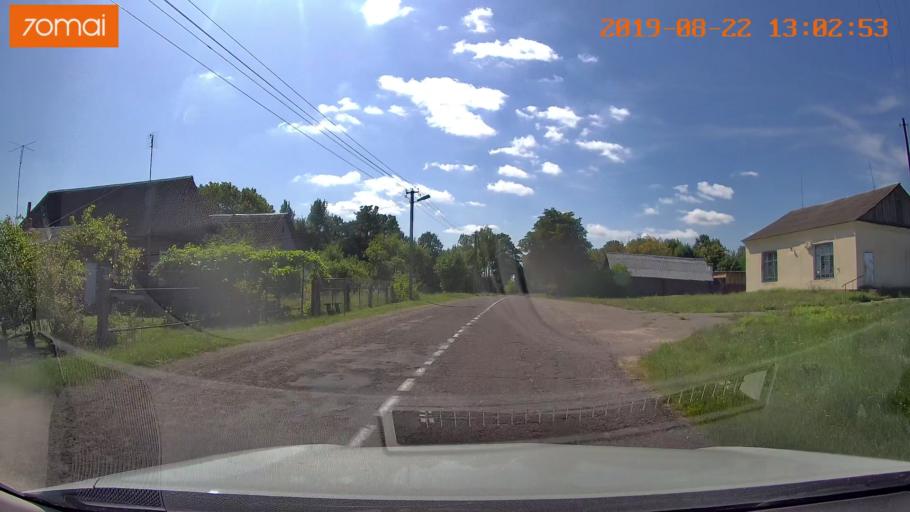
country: BY
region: Minsk
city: Prawdzinski
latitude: 53.3847
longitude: 27.8249
